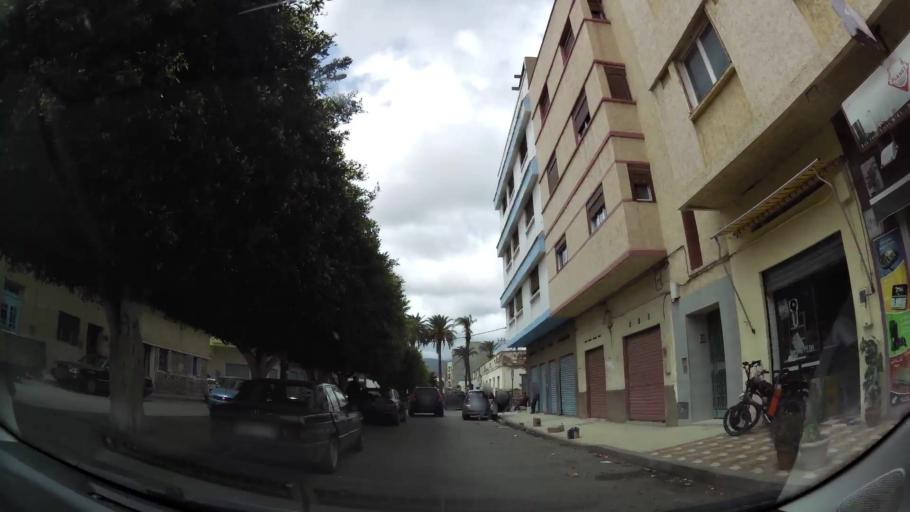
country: MA
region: Oriental
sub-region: Nador
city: Nador
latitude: 35.1796
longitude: -2.9245
